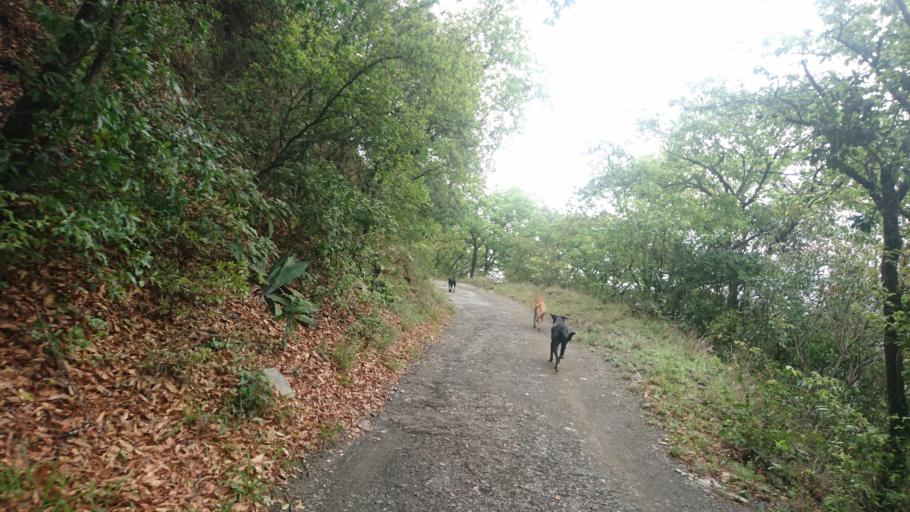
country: MX
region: Nuevo Leon
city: Garza Garcia
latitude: 25.6054
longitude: -100.3415
